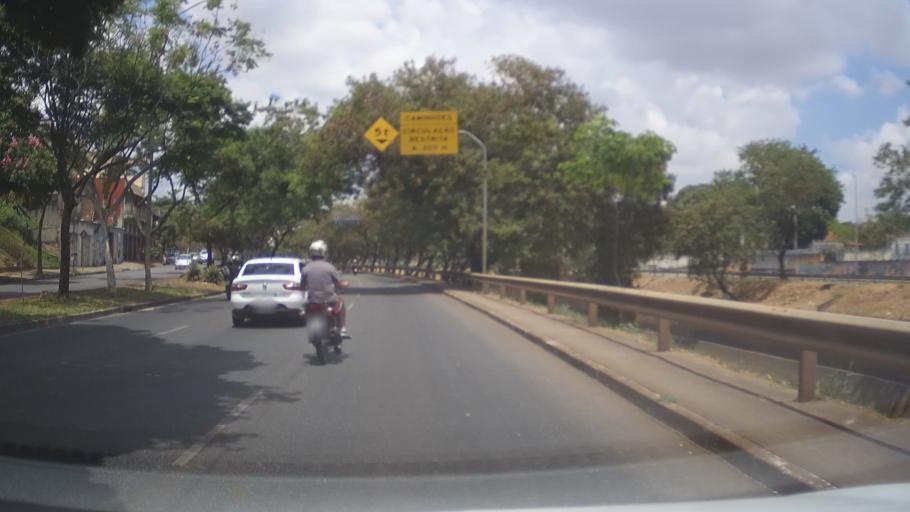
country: BR
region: Minas Gerais
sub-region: Belo Horizonte
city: Belo Horizonte
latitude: -19.9044
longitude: -43.9095
